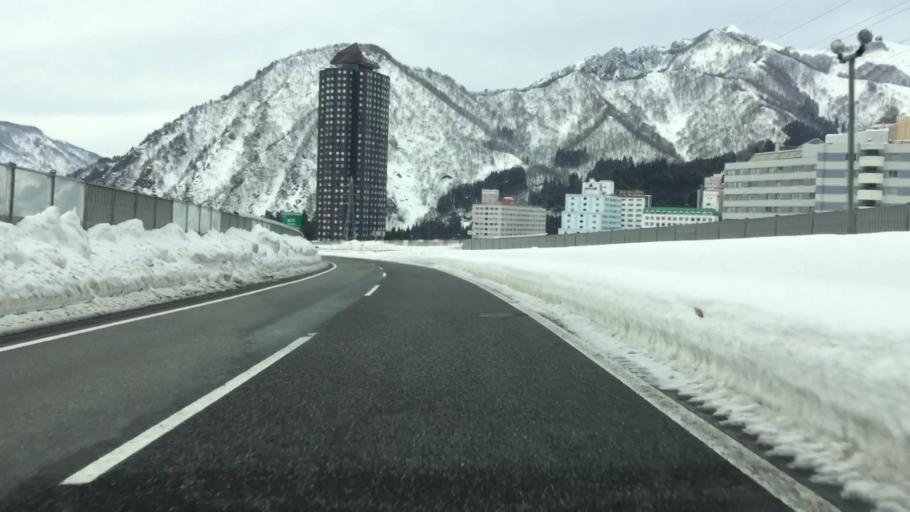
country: JP
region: Niigata
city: Shiozawa
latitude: 36.9267
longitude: 138.8406
